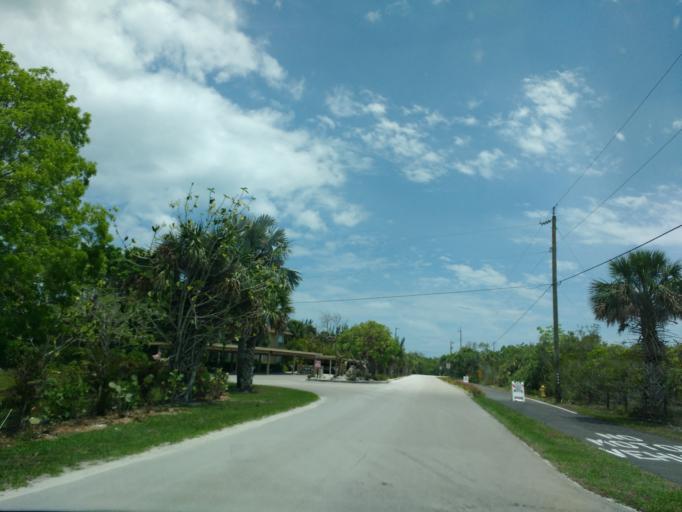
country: US
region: Florida
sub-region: Lee County
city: Saint James City
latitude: 26.4624
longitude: -82.1526
